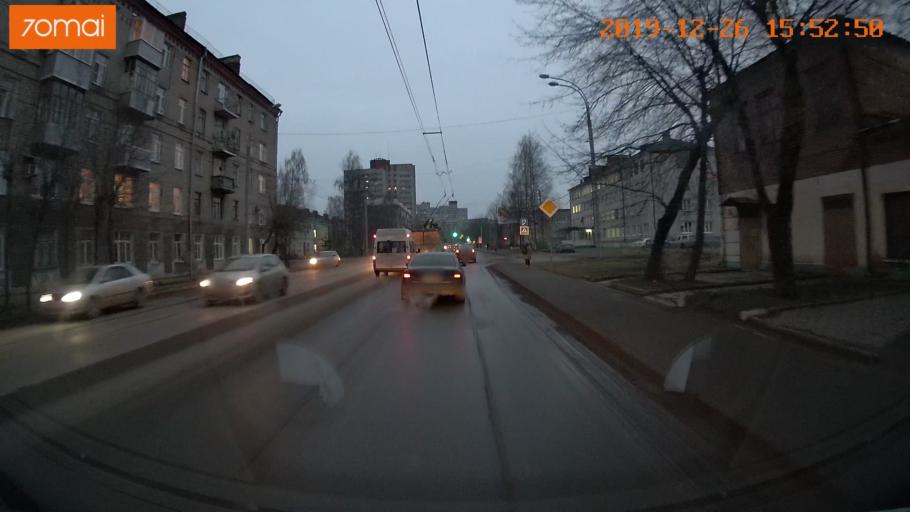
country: RU
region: Jaroslavl
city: Rybinsk
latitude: 58.0503
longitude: 38.8241
